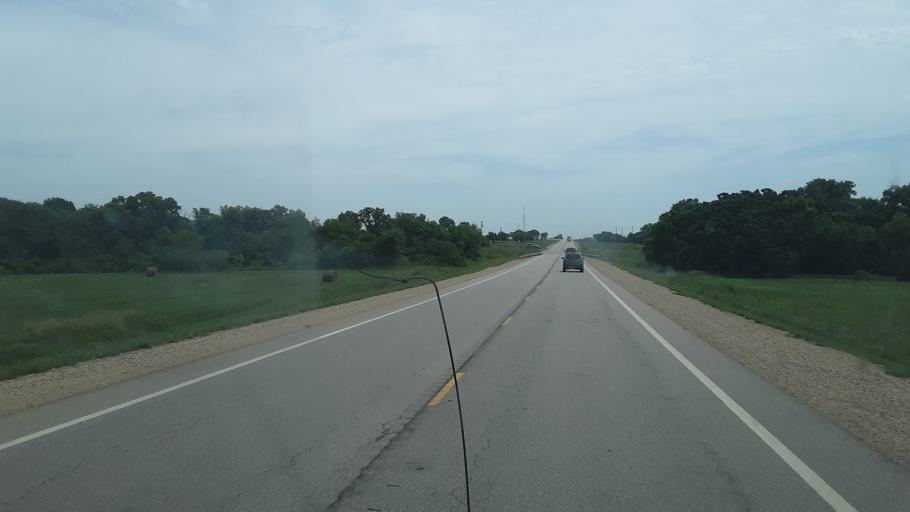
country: US
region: Kansas
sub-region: Greenwood County
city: Eureka
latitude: 37.8134
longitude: -96.4648
